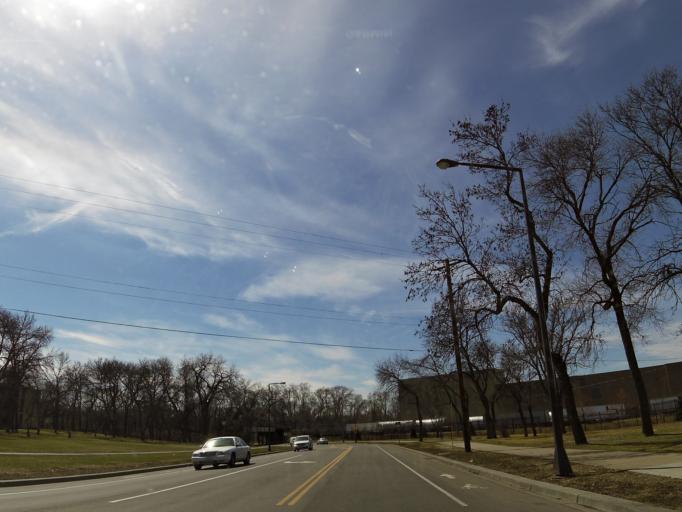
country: US
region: Minnesota
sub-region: Ramsey County
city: Maplewood
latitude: 44.9712
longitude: -93.0443
